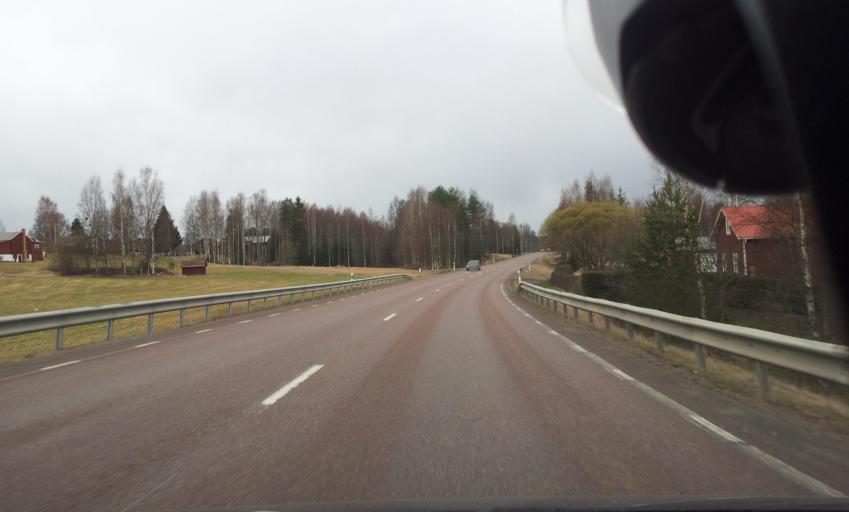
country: SE
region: Gaevleborg
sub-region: Ljusdals Kommun
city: Farila
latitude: 61.8096
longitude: 15.9527
